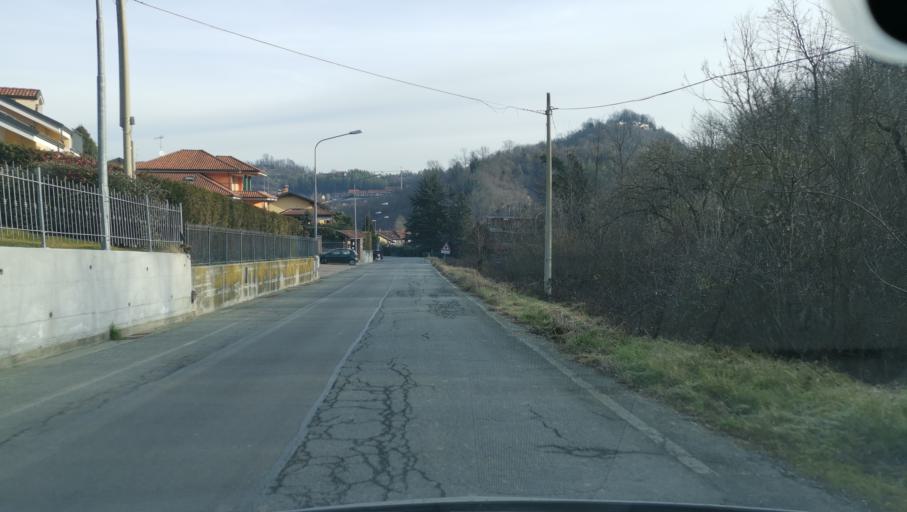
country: IT
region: Piedmont
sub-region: Provincia di Torino
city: Castiglione Torinese
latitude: 45.1042
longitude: 7.8142
